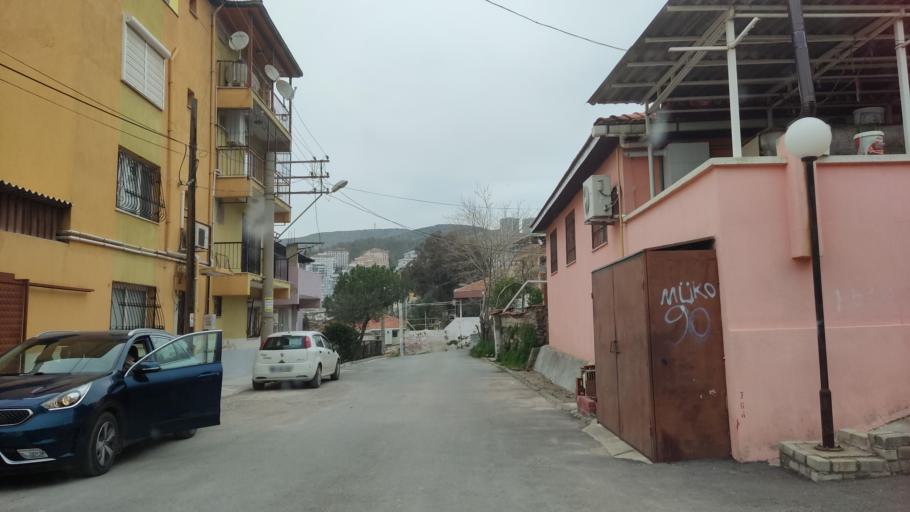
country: TR
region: Izmir
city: Karsiyaka
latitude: 38.4969
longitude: 27.0691
